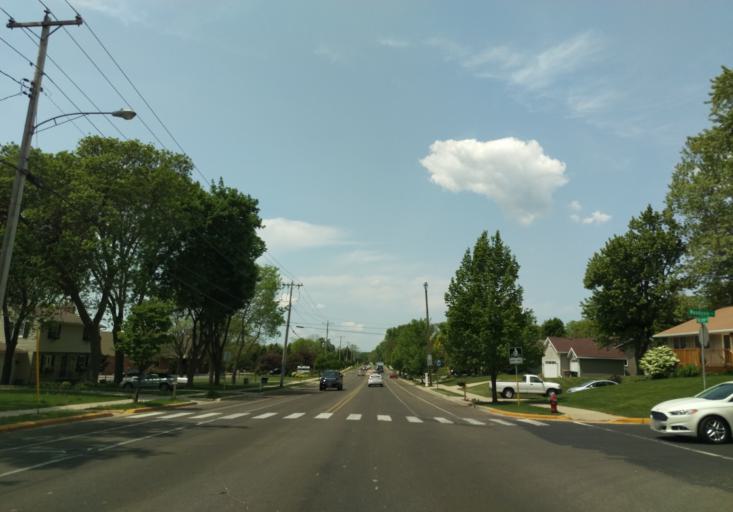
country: US
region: Wisconsin
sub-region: Dane County
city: Monona
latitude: 43.0734
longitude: -89.2955
